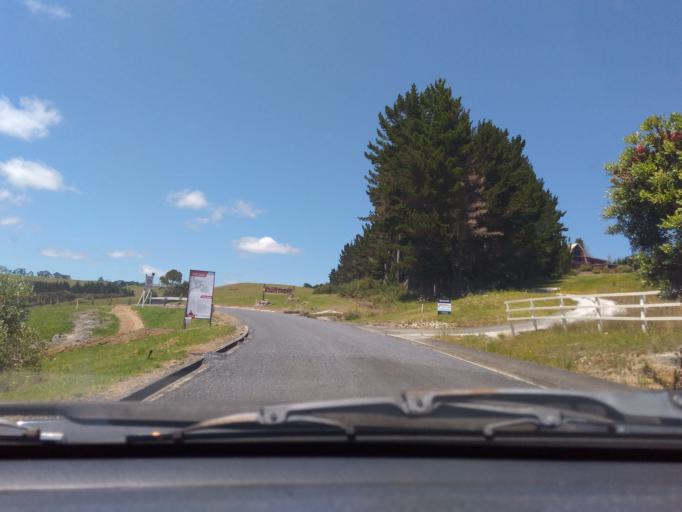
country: NZ
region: Northland
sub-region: Far North District
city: Taipa
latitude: -34.9953
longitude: 173.5113
